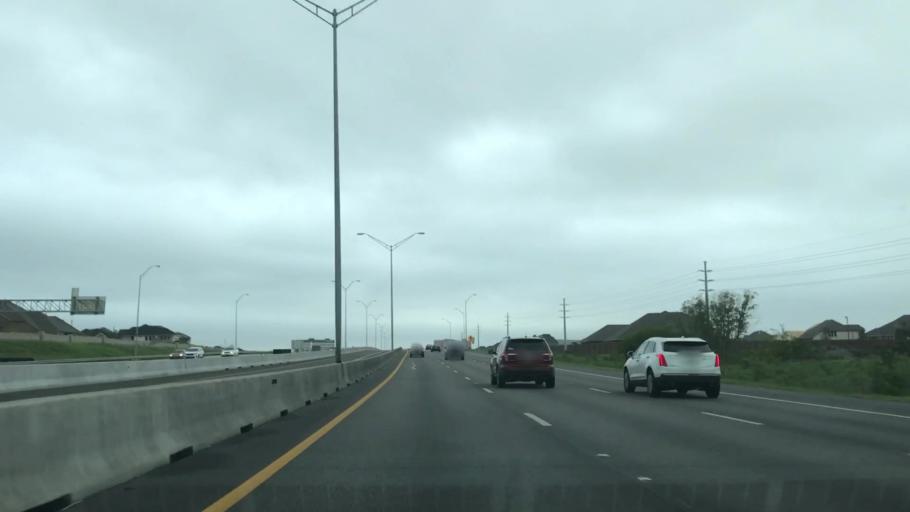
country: US
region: Texas
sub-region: Dallas County
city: Coppell
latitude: 32.9067
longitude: -96.9940
